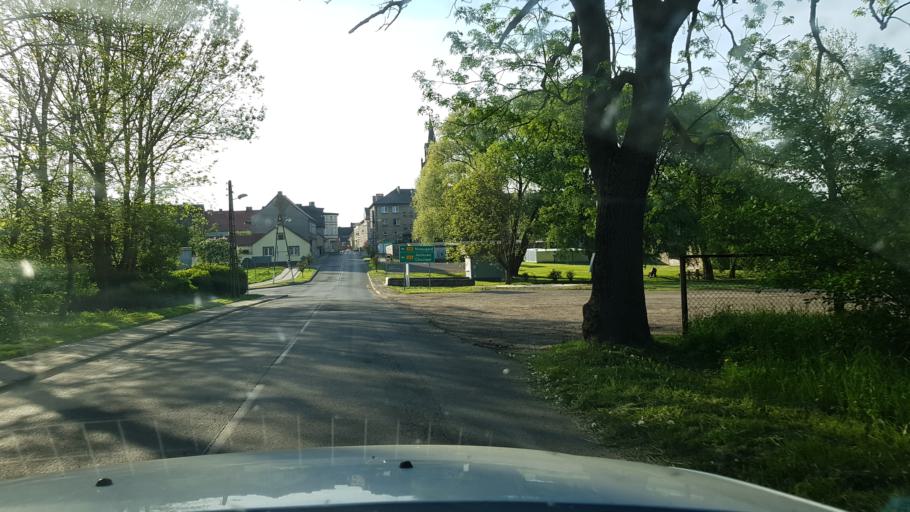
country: PL
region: West Pomeranian Voivodeship
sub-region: Powiat lobeski
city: Dobra
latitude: 53.5853
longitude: 15.3119
